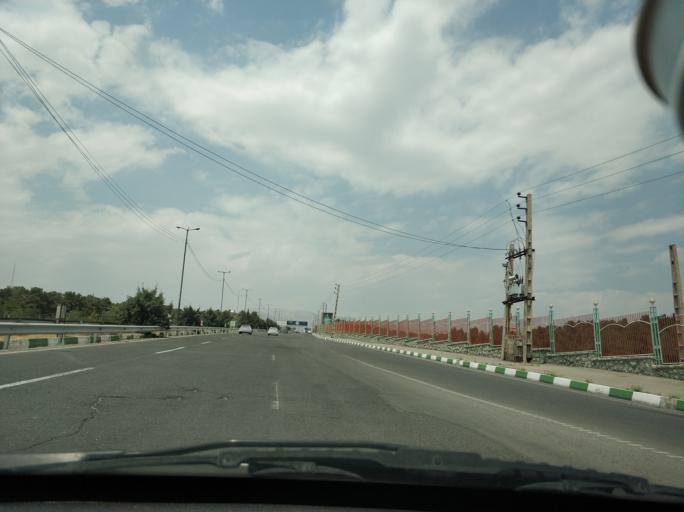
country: IR
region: Tehran
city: Tajrish
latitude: 35.7725
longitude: 51.5588
